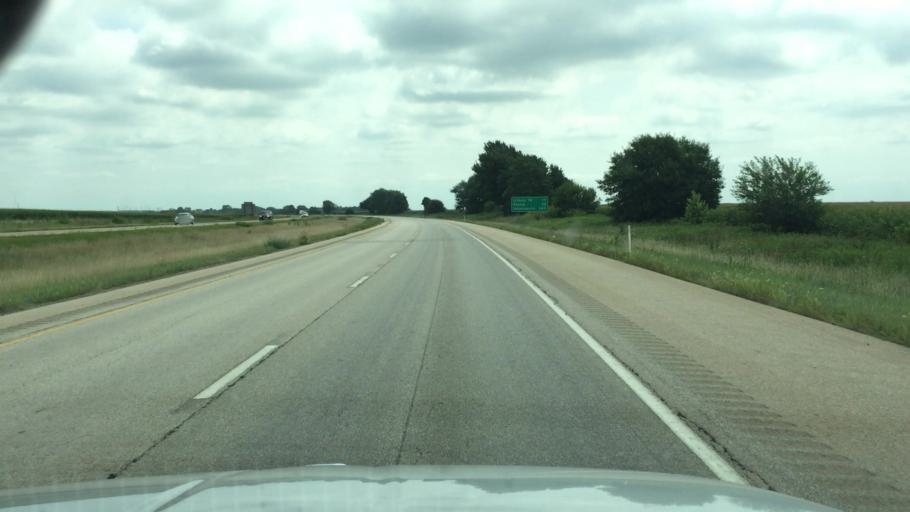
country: US
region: Illinois
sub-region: Knox County
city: Knoxville
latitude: 40.9039
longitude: -90.2335
